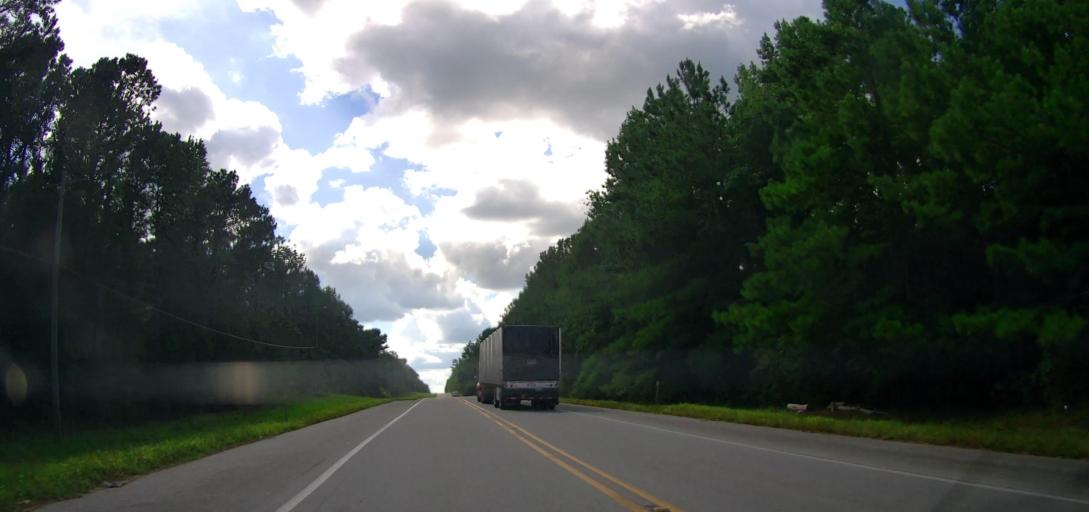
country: US
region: Alabama
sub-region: Lee County
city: Auburn
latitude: 32.4409
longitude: -85.4933
